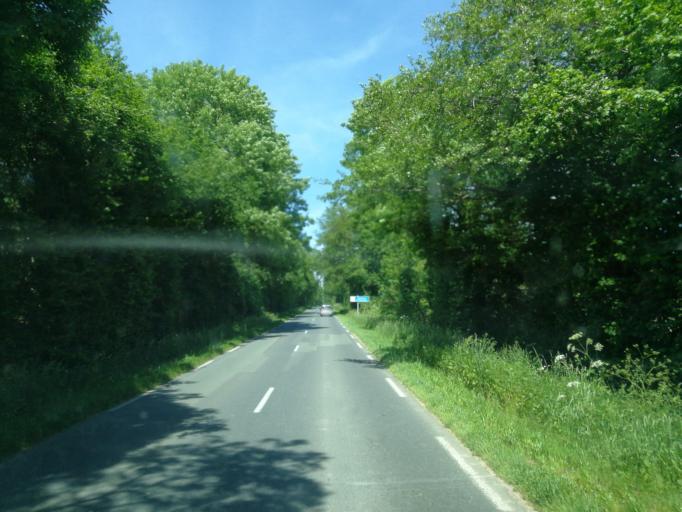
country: FR
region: Pays de la Loire
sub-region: Departement de la Vendee
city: Saint-Pierre-du-Chemin
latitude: 46.7240
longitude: -0.6757
